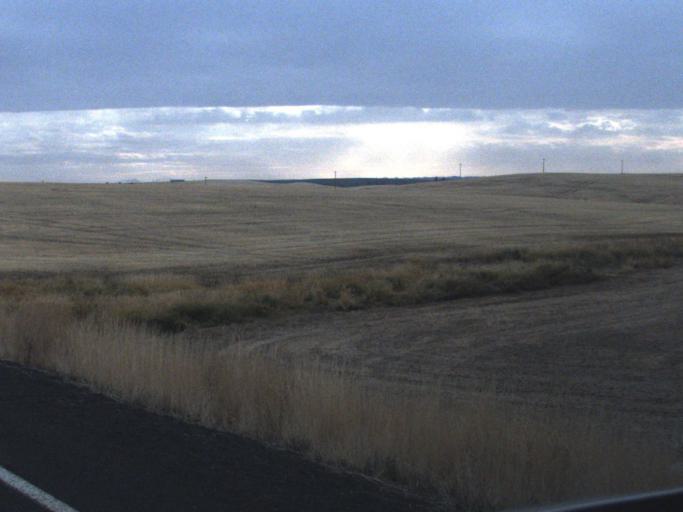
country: US
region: Washington
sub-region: Lincoln County
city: Davenport
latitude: 47.8429
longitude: -118.2130
